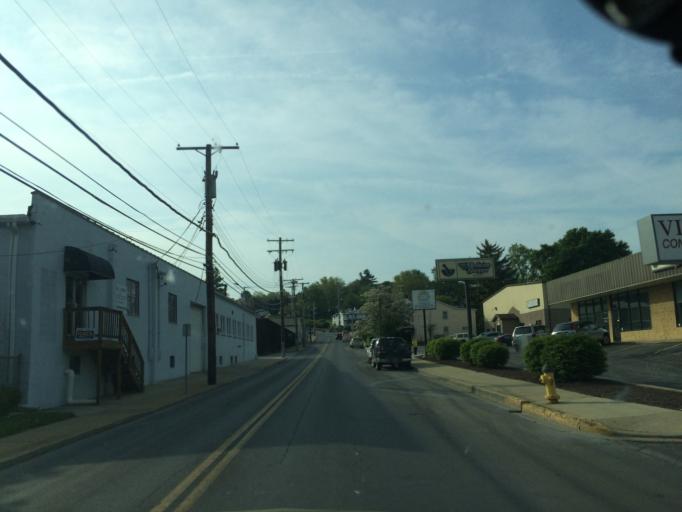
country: US
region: Maryland
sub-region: Carroll County
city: Westminster
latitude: 39.5666
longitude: -76.9892
